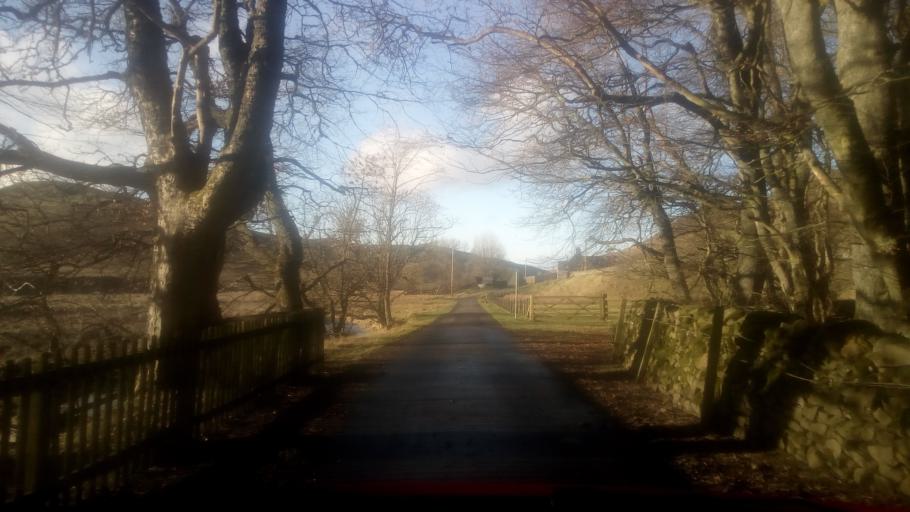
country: GB
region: England
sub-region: Northumberland
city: Rochester
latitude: 55.3875
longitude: -2.3735
